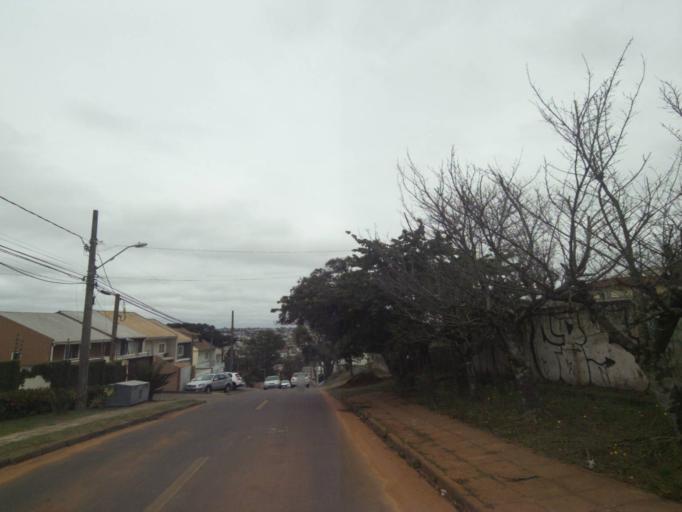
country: BR
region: Parana
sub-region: Pinhais
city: Pinhais
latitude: -25.4805
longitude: -49.2341
